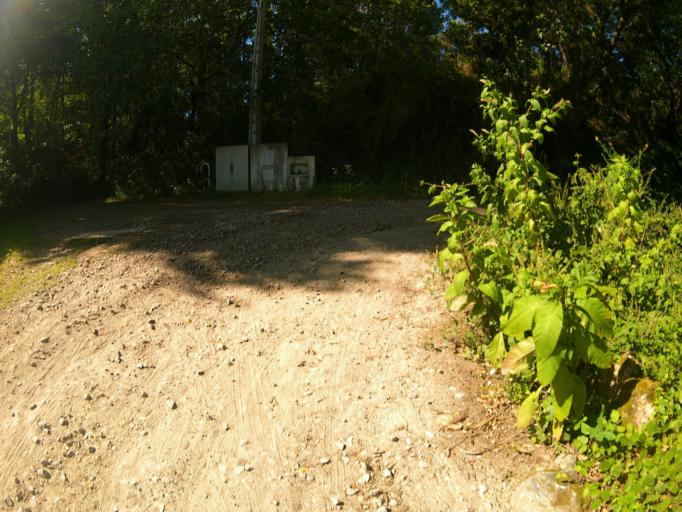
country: PT
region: Viana do Castelo
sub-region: Ponte de Lima
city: Ponte de Lima
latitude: 41.7269
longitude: -8.6688
